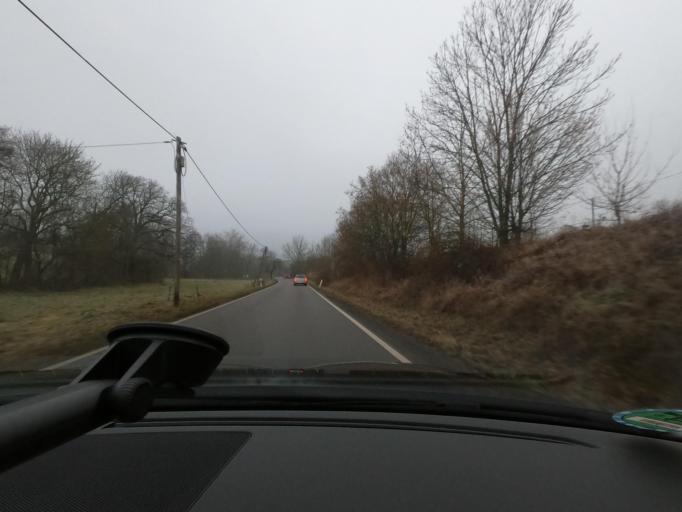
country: DE
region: Thuringia
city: Dornheim
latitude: 50.8141
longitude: 11.0103
